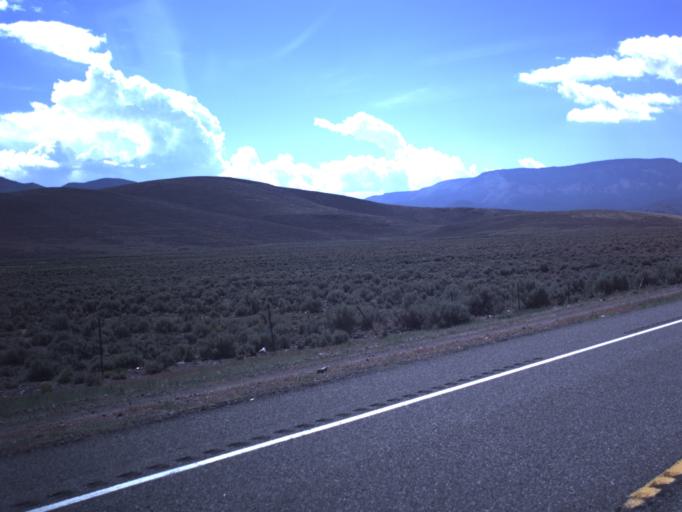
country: US
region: Utah
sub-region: Piute County
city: Junction
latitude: 38.2693
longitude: -112.2224
